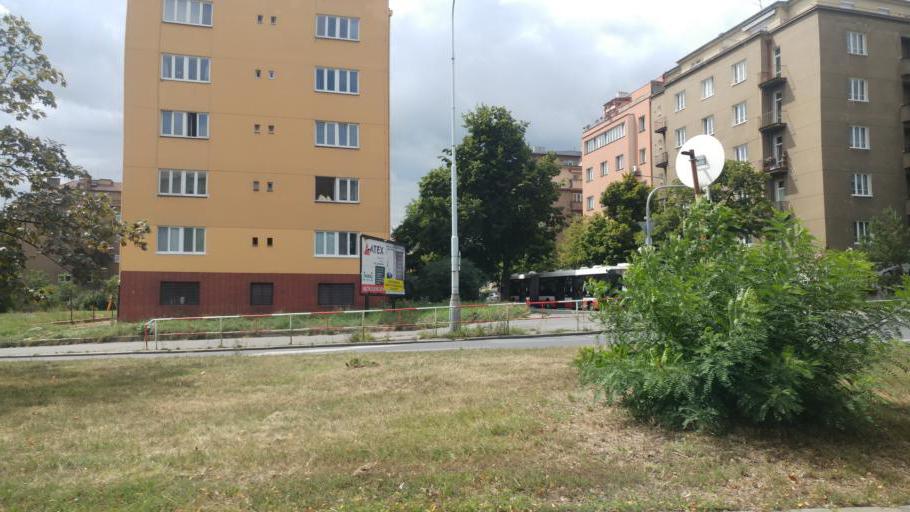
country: CZ
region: Praha
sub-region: Praha 8
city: Karlin
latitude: 50.0719
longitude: 14.4710
